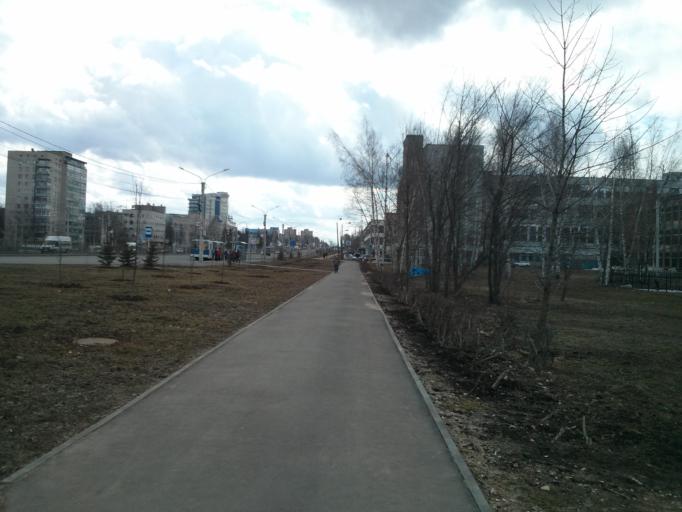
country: RU
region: Chuvashia
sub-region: Cheboksarskiy Rayon
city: Cheboksary
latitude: 56.1069
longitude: 47.2607
